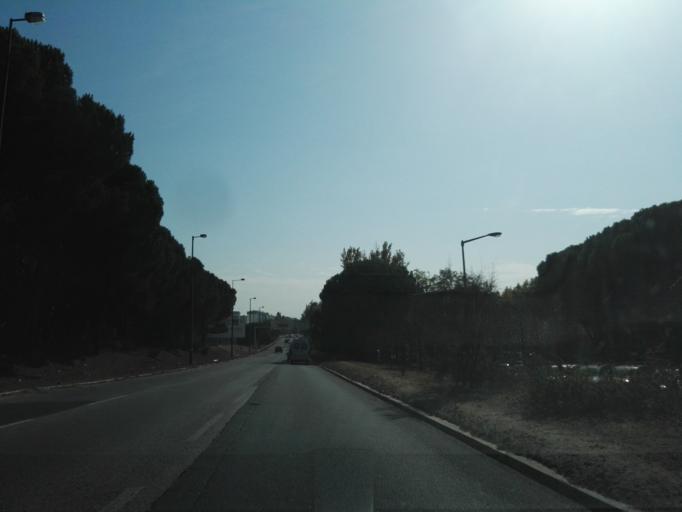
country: PT
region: Lisbon
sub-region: Loures
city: Moscavide
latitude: 38.7743
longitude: -9.1238
